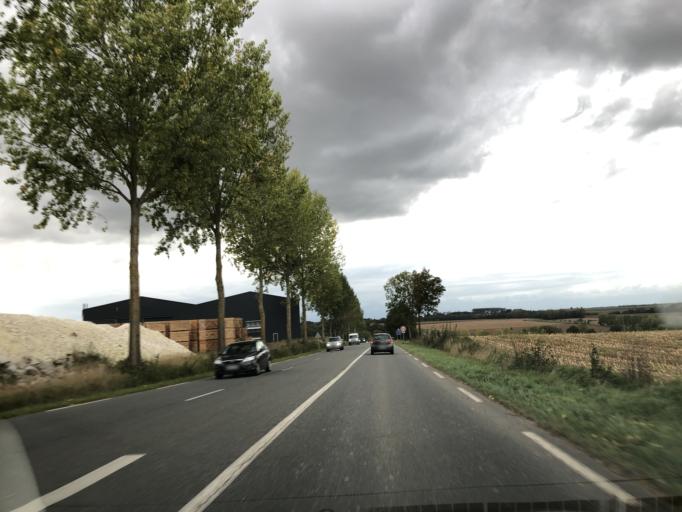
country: FR
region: Picardie
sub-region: Departement de la Somme
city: Chepy
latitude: 50.0990
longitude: 1.7299
